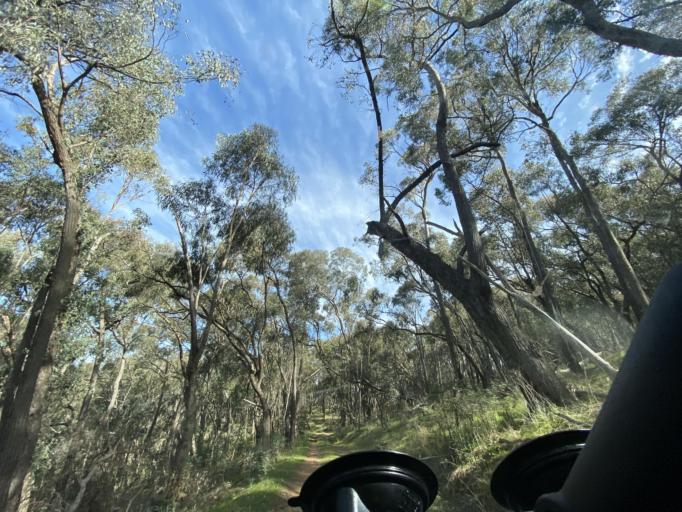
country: AU
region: Victoria
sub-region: Mansfield
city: Mansfield
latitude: -36.8052
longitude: 146.1191
